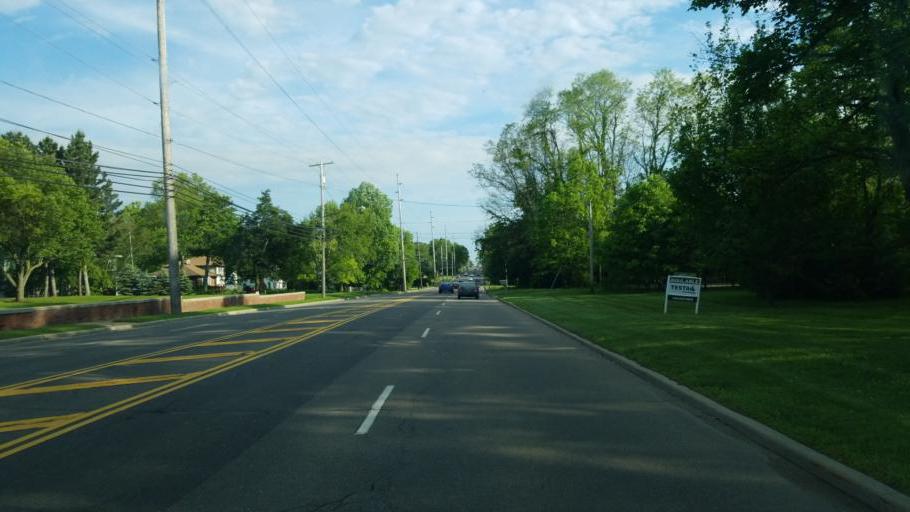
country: US
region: Ohio
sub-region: Summit County
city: Stow
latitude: 41.1821
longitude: -81.4405
